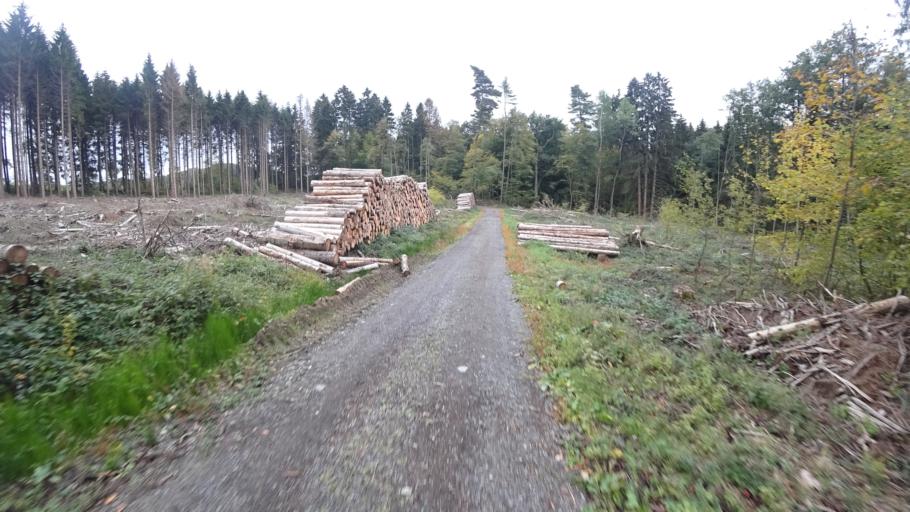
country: DE
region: Rheinland-Pfalz
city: Nordhofen
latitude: 50.5258
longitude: 7.7357
